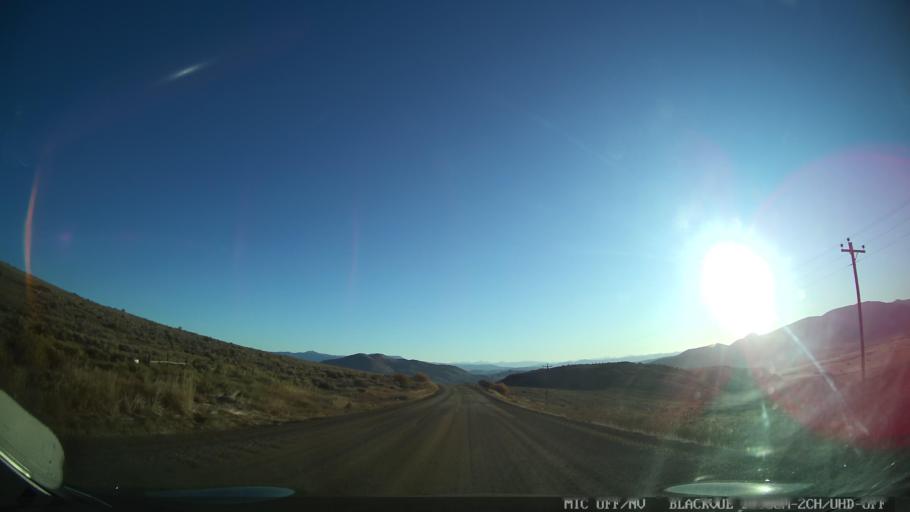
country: US
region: Colorado
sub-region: Grand County
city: Kremmling
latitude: 39.9940
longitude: -106.4126
